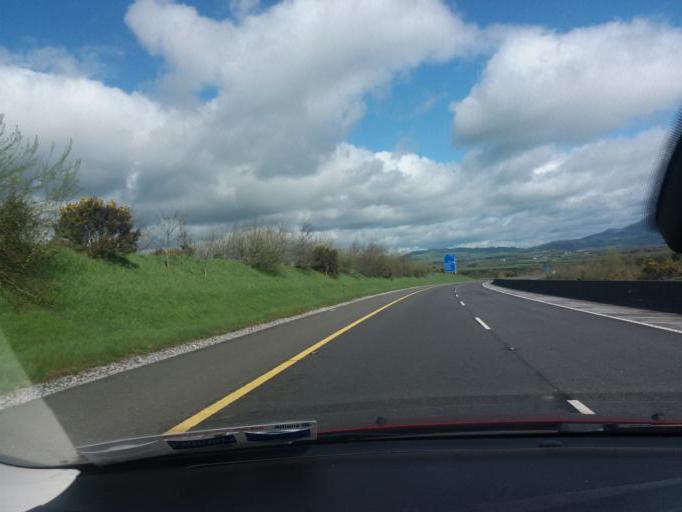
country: IE
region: Munster
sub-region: County Cork
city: Mitchelstown
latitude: 52.2230
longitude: -8.2875
